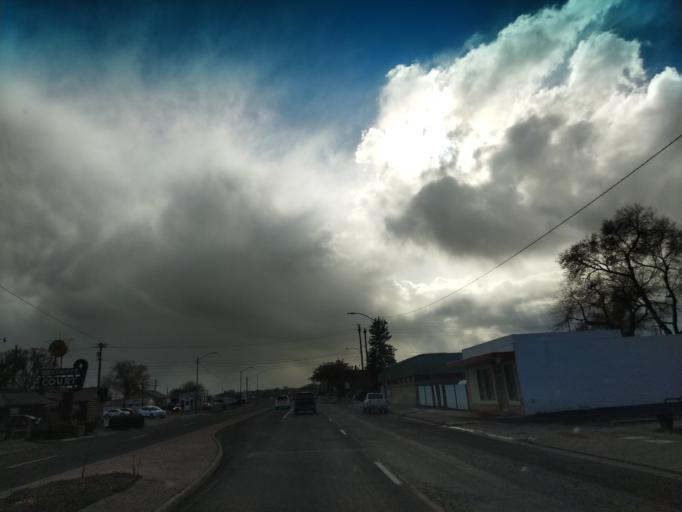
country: US
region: Colorado
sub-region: Delta County
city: Delta
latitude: 38.7335
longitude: -108.0708
